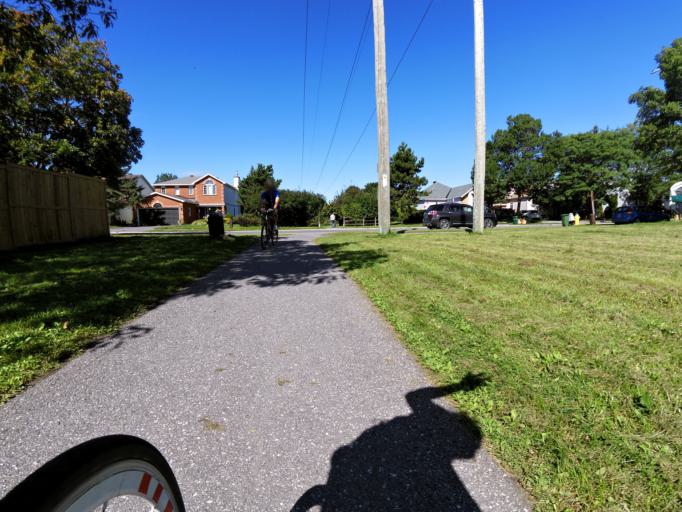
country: CA
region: Ontario
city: Bells Corners
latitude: 45.2956
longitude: -75.8607
